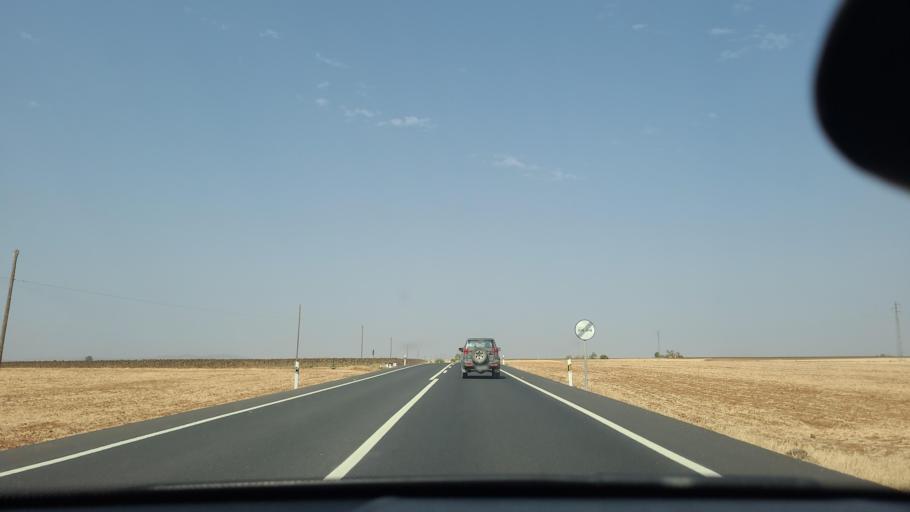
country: ES
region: Extremadura
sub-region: Provincia de Badajoz
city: Berlanga
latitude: 38.2652
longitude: -5.7537
